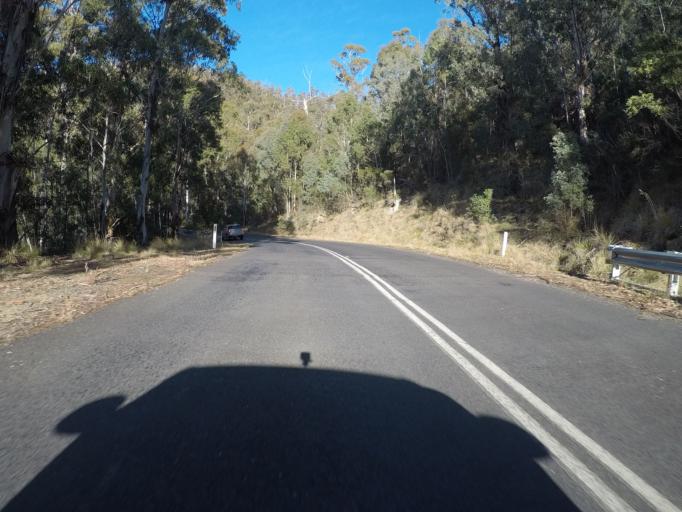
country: AU
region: Australian Capital Territory
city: Macarthur
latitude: -35.4864
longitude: 148.9319
